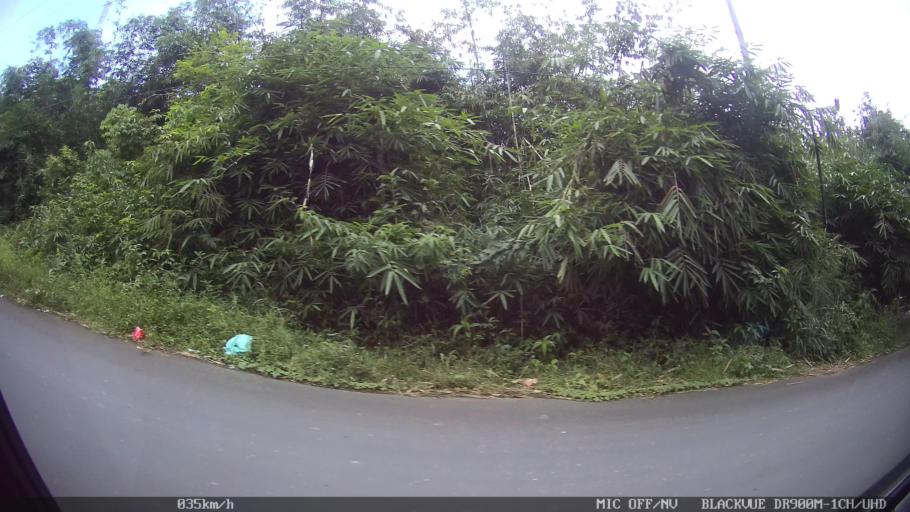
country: ID
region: Lampung
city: Bandarlampung
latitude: -5.4280
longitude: 105.1995
